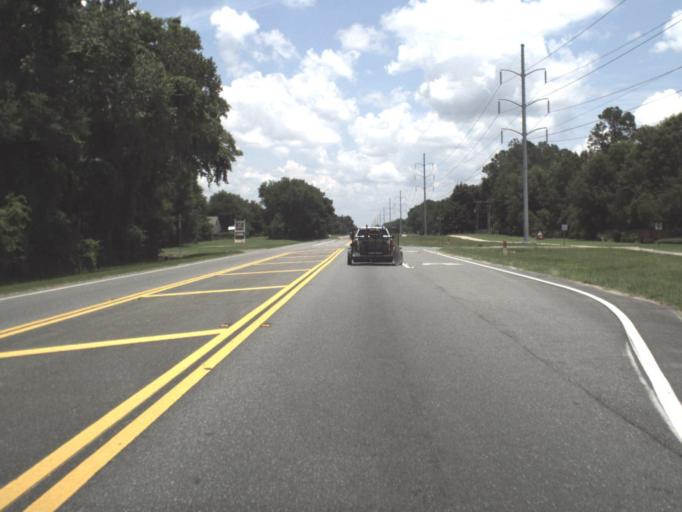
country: US
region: Florida
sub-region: Alachua County
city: Archer
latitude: 29.5920
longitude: -82.4345
